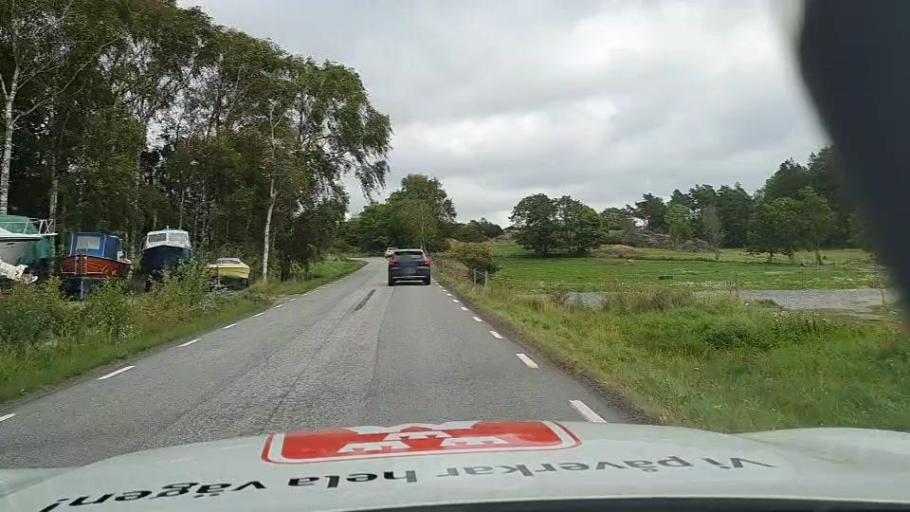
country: SE
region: Vaestra Goetaland
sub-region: Orust
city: Henan
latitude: 58.1593
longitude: 11.5969
